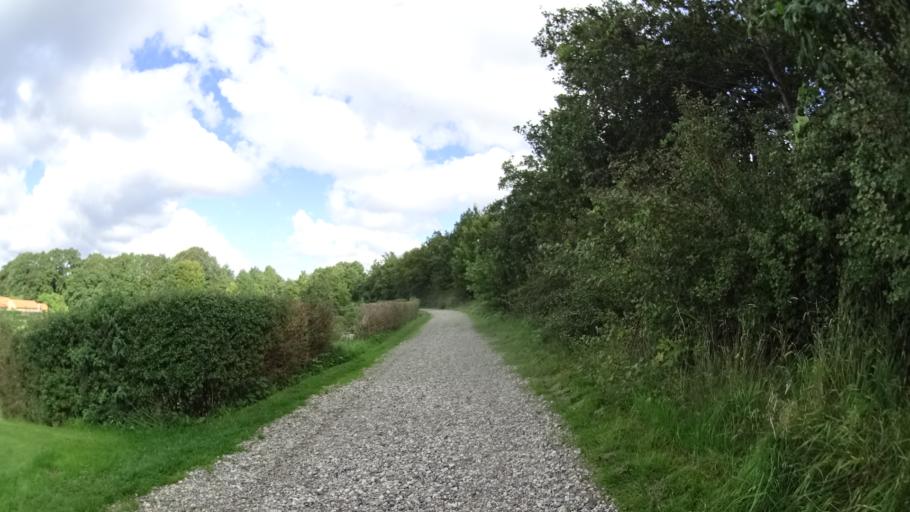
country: DK
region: Central Jutland
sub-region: Arhus Kommune
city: Arhus
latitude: 56.1123
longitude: 10.1889
